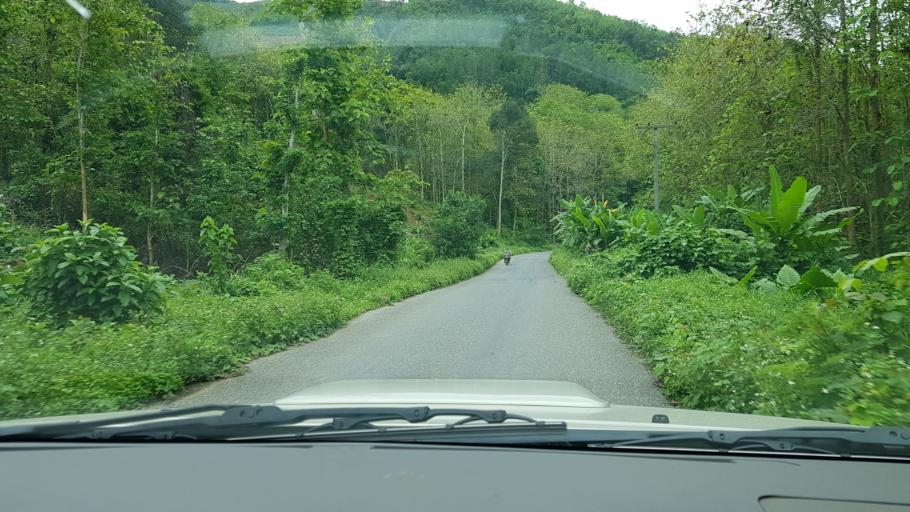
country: LA
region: Phongsali
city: Khoa
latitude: 21.0603
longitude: 102.3859
